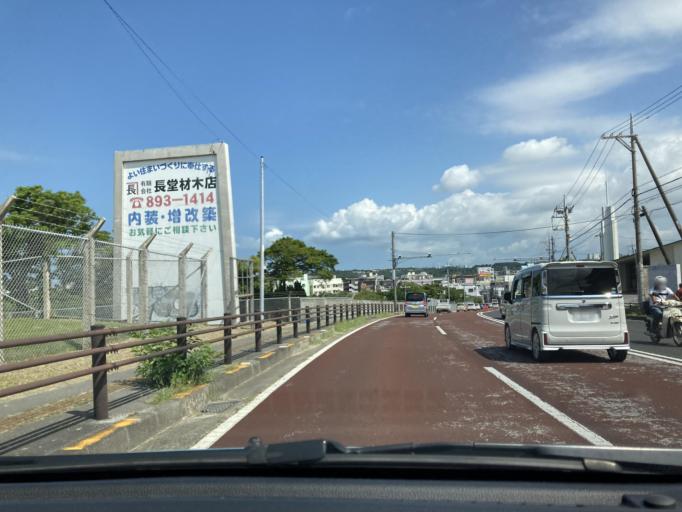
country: JP
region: Okinawa
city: Chatan
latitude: 26.2855
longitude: 127.7764
